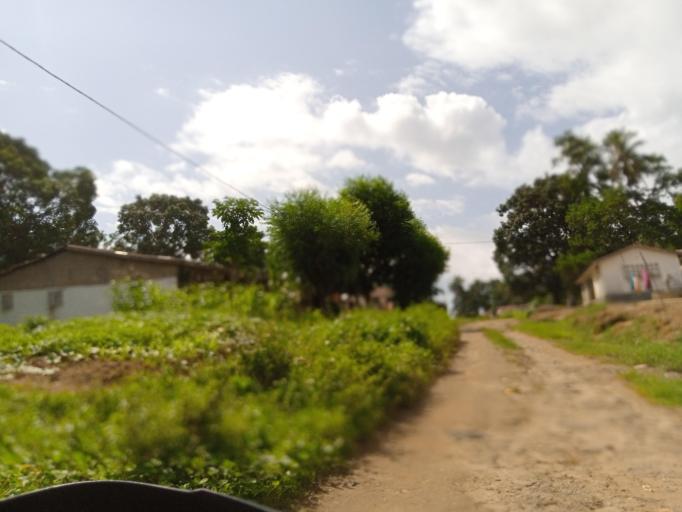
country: SL
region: Northern Province
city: Masoyila
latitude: 8.6073
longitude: -13.2053
